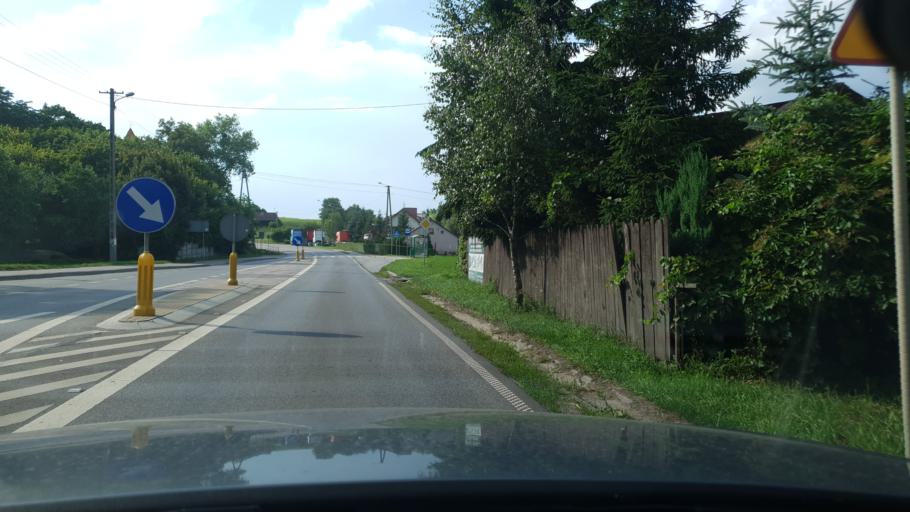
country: PL
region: Kujawsko-Pomorskie
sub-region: Powiat grudziadzki
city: Gruta
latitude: 53.4355
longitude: 18.8957
